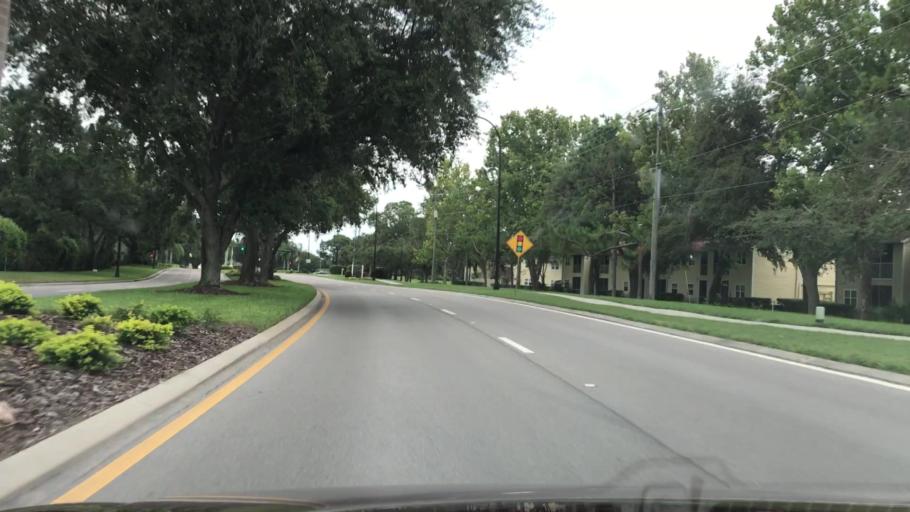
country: US
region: Florida
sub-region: Sarasota County
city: Vamo
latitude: 27.2349
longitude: -82.4852
